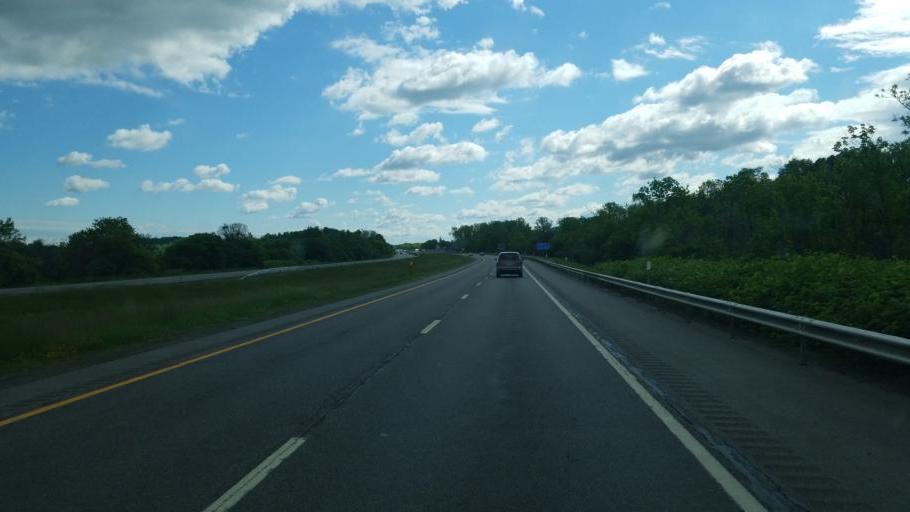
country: US
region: New York
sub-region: Cayuga County
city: Port Byron
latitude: 43.0325
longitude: -76.6472
